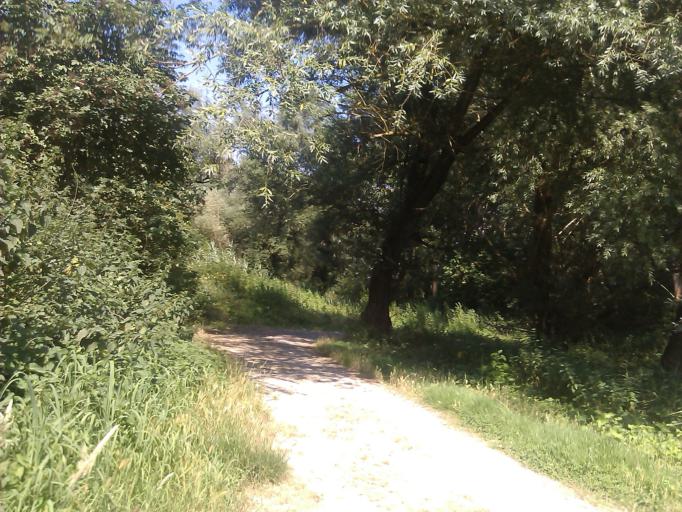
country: IT
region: Tuscany
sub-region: Provincia di Siena
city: Chiusi
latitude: 43.0524
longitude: 11.9534
